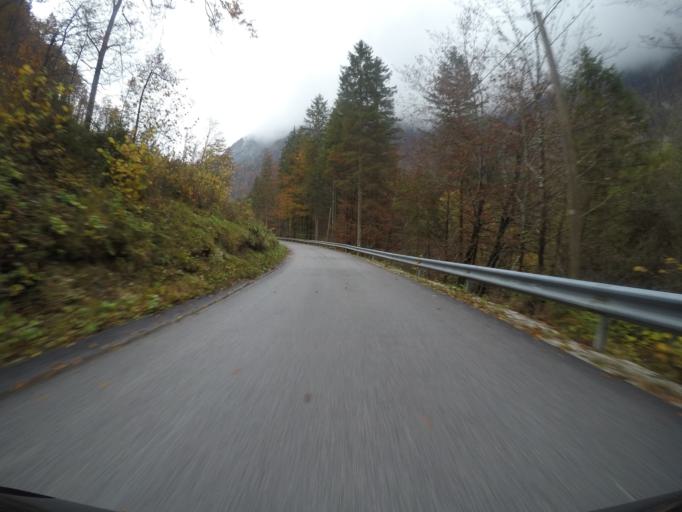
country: SI
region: Jesenice
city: Hrusica
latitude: 46.3985
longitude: 14.0011
